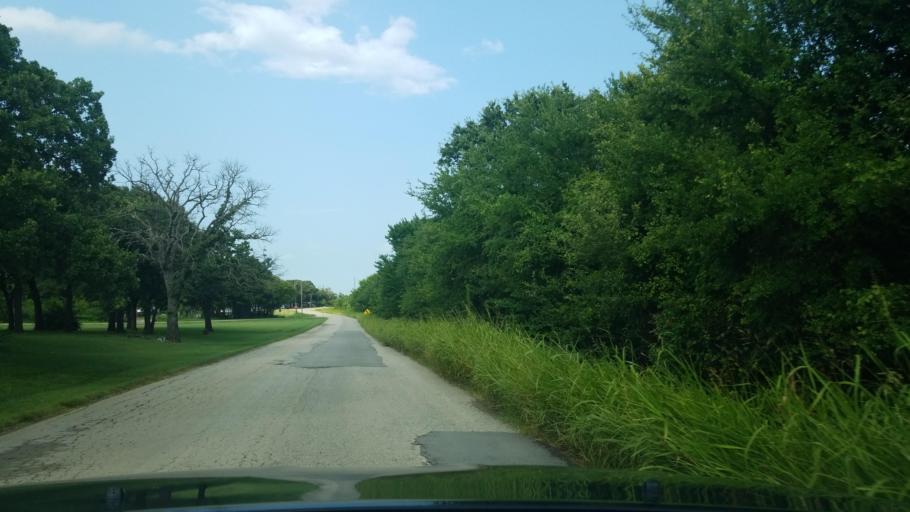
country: US
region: Texas
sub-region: Denton County
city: Denton
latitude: 33.2398
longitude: -97.0792
